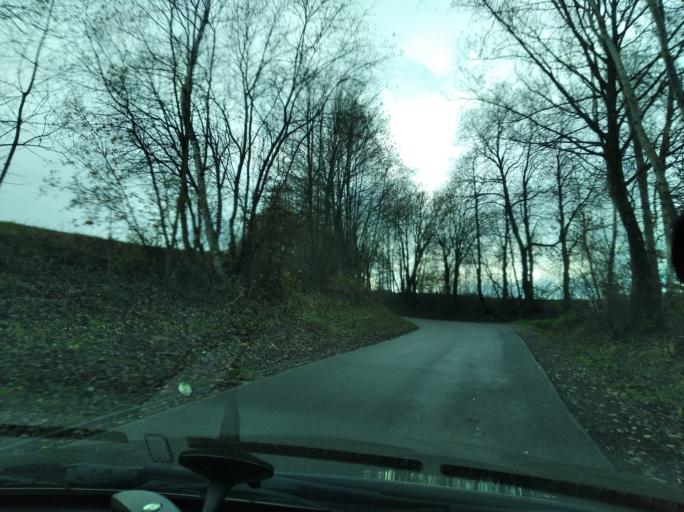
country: PL
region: Subcarpathian Voivodeship
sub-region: Powiat strzyzowski
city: Strzyzow
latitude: 49.9262
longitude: 21.7728
